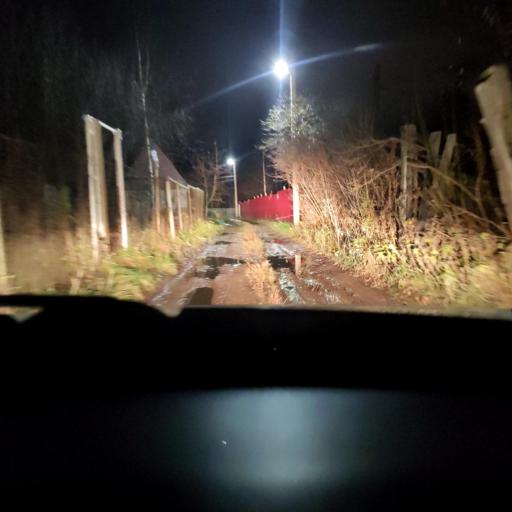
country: RU
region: Perm
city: Froly
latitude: 57.9482
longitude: 56.2436
